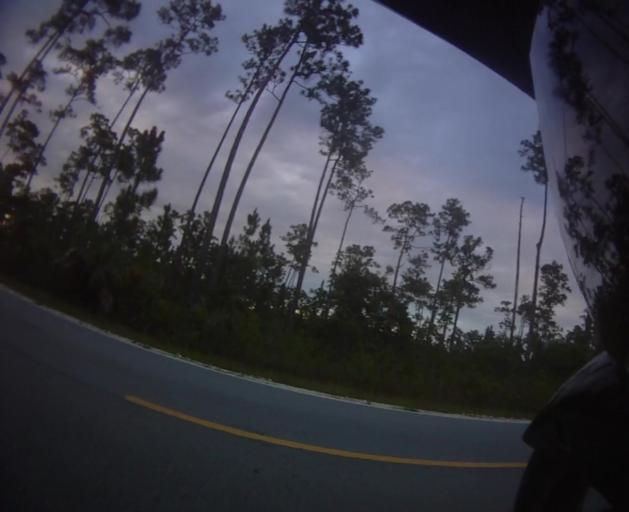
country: US
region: Florida
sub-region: Miami-Dade County
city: Florida City
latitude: 25.3893
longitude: -80.6434
